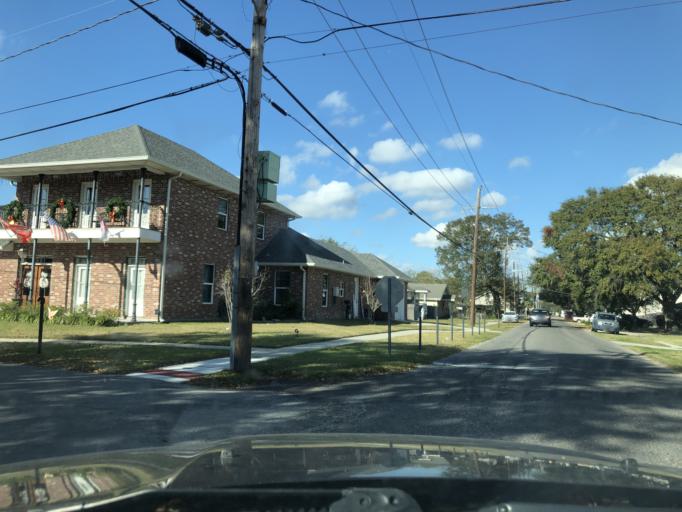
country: US
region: Louisiana
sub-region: Jefferson Parish
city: Metairie Terrace
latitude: 29.9802
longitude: -90.1673
